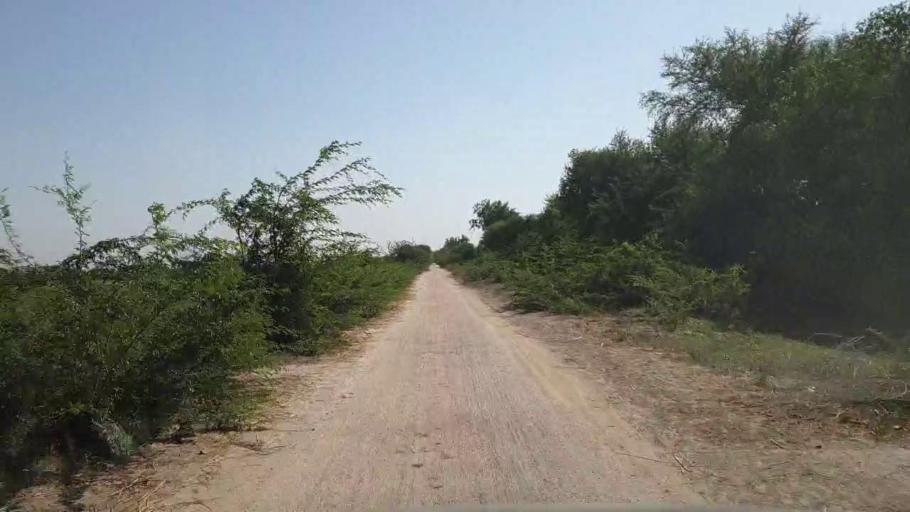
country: PK
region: Sindh
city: Tando Bago
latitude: 24.6535
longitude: 68.9820
